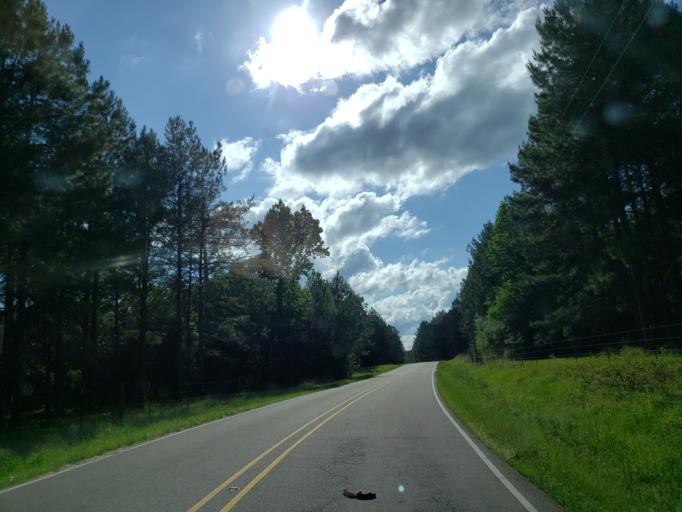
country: US
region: Mississippi
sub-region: Lamar County
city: Sumrall
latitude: 31.3536
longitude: -89.4884
